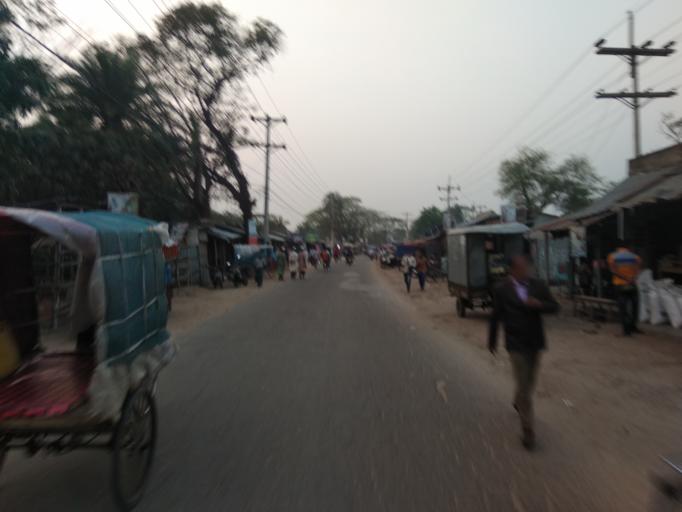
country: IN
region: West Bengal
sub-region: North 24 Parganas
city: Taki
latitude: 22.4531
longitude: 89.0352
